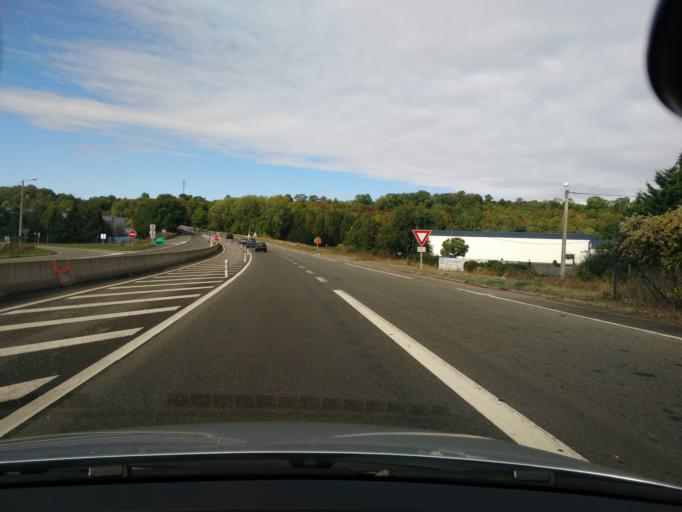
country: FR
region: Centre
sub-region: Departement d'Eure-et-Loir
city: Dreux
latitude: 48.7463
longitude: 1.3872
